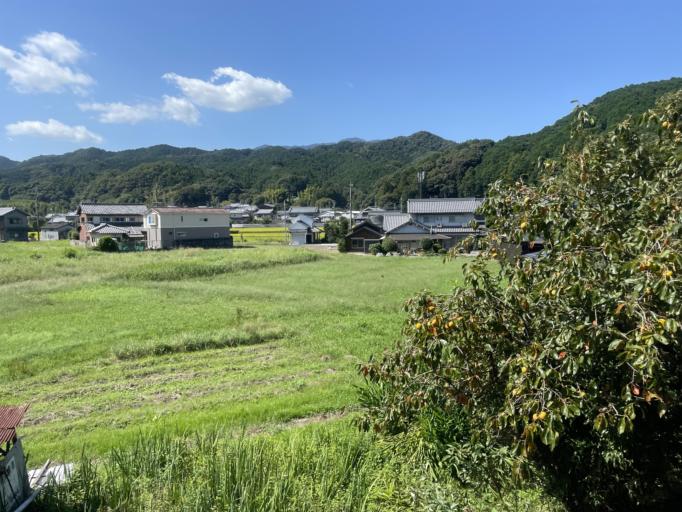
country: JP
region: Nara
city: Gose
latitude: 34.4139
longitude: 135.7484
